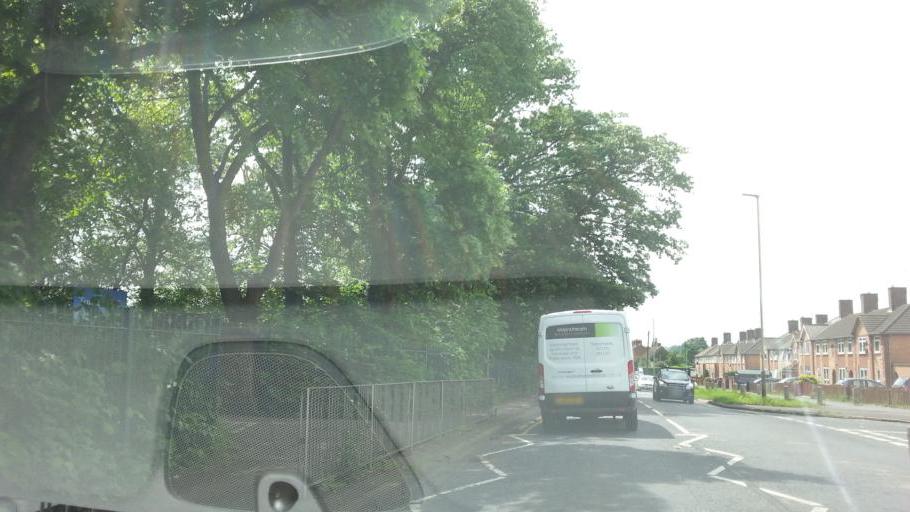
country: GB
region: England
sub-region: City of Leicester
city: Leicester
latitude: 52.6502
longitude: -1.0938
